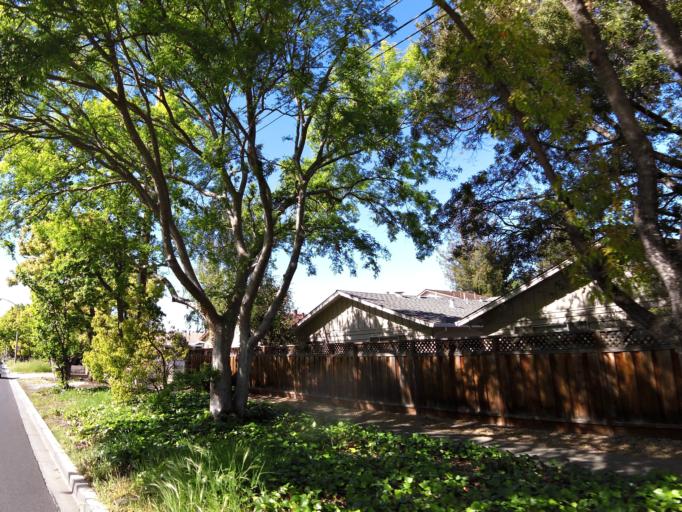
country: US
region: California
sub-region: Santa Clara County
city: Palo Alto
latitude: 37.4207
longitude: -122.1277
